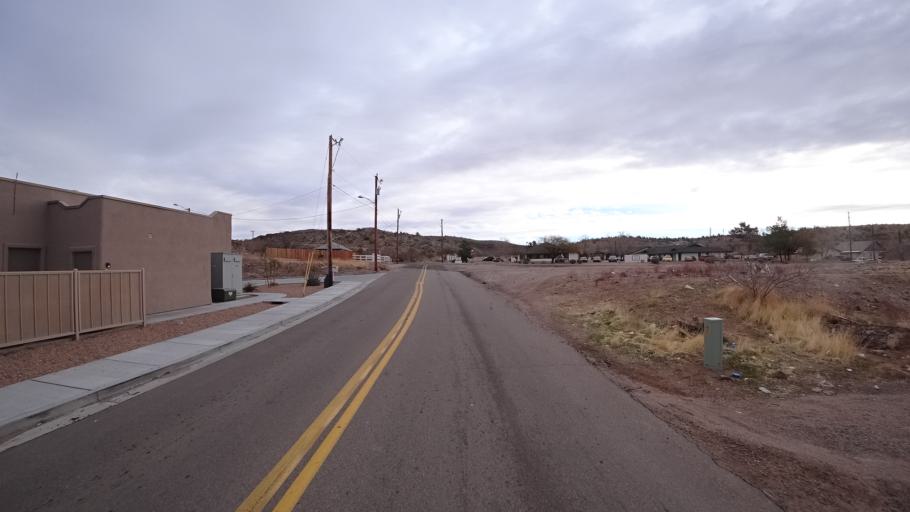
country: US
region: Arizona
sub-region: Mohave County
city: Kingman
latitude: 35.1973
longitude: -114.0757
